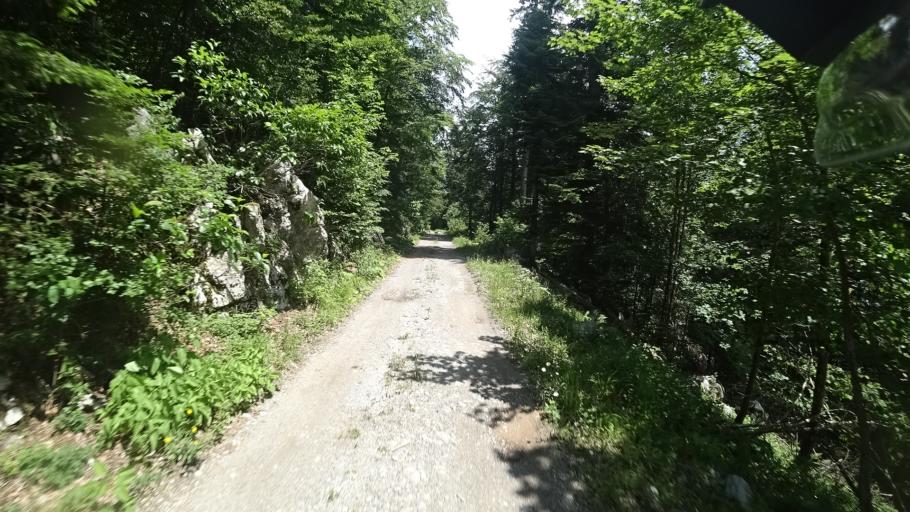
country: SI
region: Osilnica
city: Osilnica
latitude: 45.4849
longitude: 14.7419
